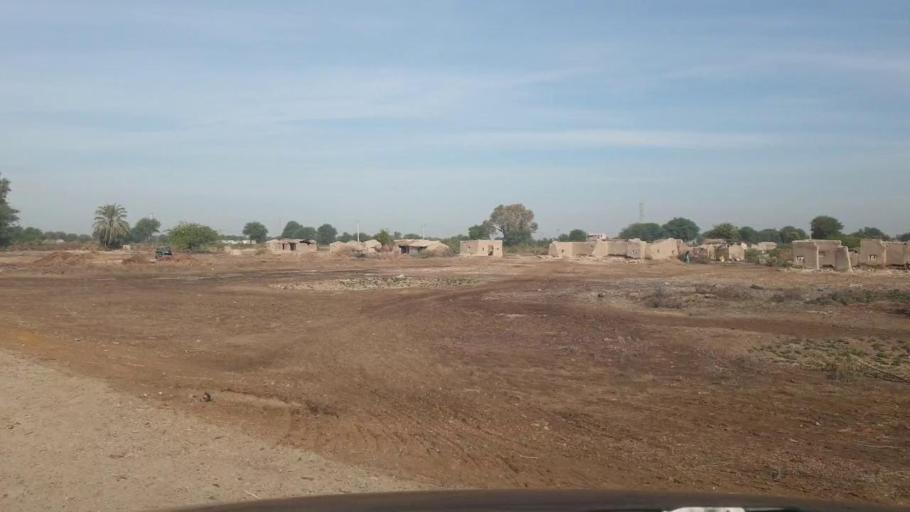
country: PK
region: Sindh
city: Umarkot
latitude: 25.3627
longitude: 69.6968
